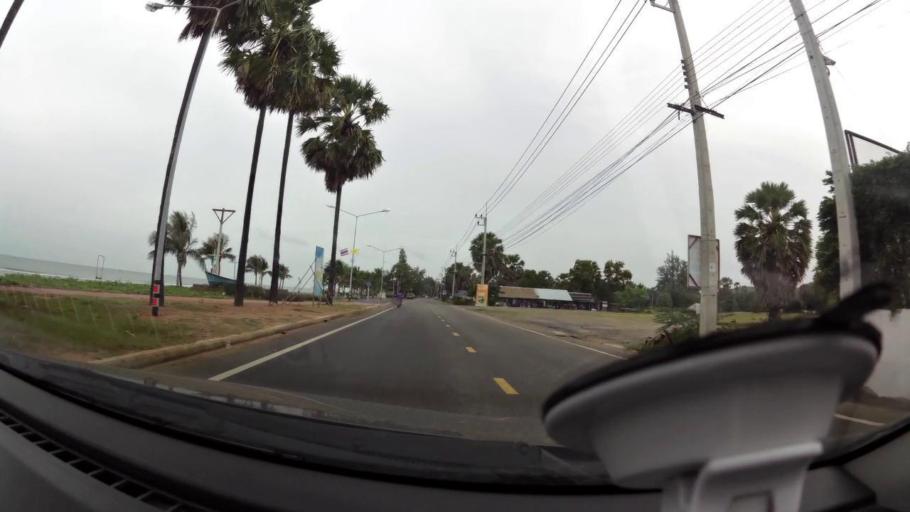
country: TH
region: Prachuap Khiri Khan
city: Pran Buri
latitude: 12.3719
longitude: 100.0000
